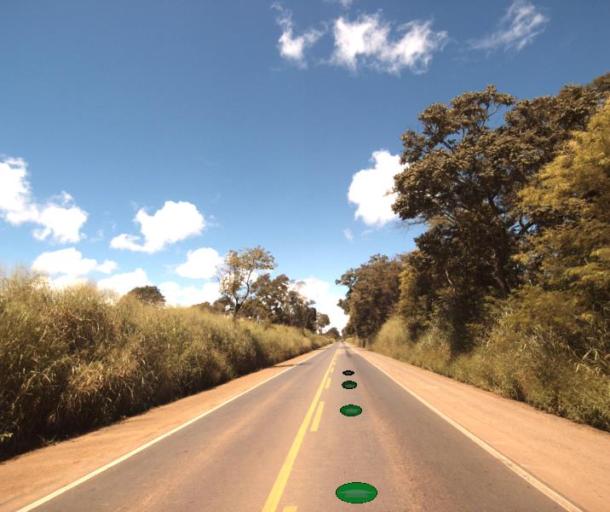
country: BR
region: Goias
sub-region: Anapolis
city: Anapolis
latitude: -16.1460
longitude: -49.0460
